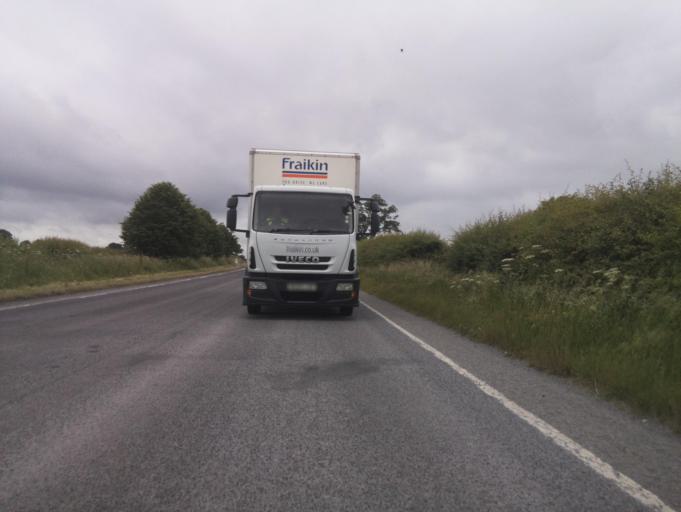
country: GB
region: England
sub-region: District of Rutland
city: Uppingham
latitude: 52.5984
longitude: -0.7328
